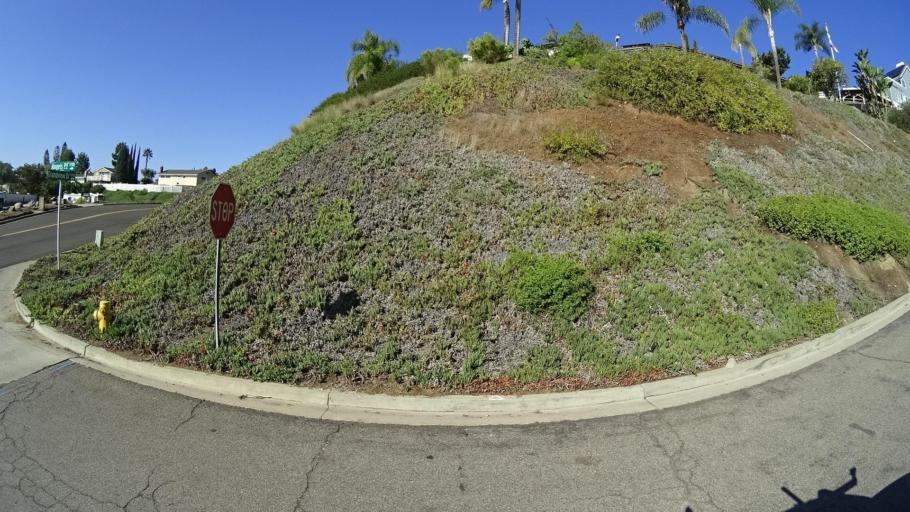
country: US
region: California
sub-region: San Diego County
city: Casa de Oro-Mount Helix
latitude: 32.7636
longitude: -116.9860
